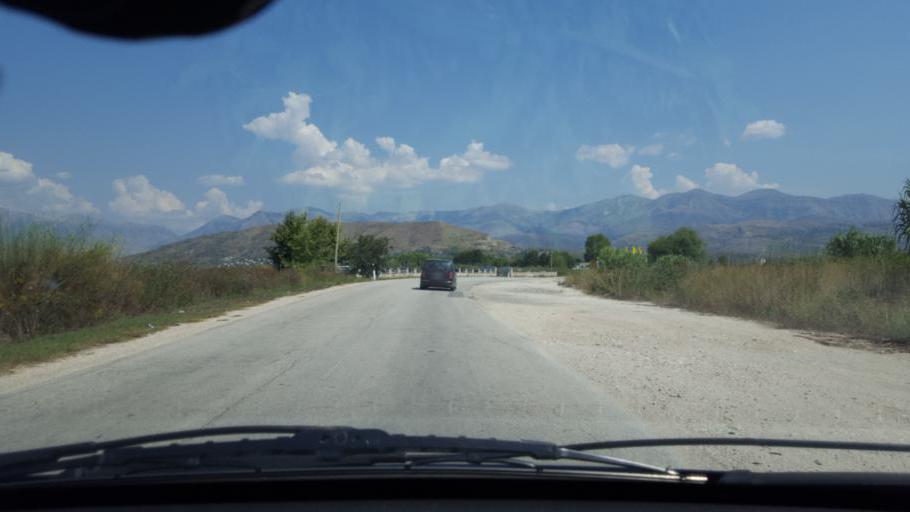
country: AL
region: Vlore
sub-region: Rrethi i Delvines
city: Finiq
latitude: 39.8834
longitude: 20.0563
